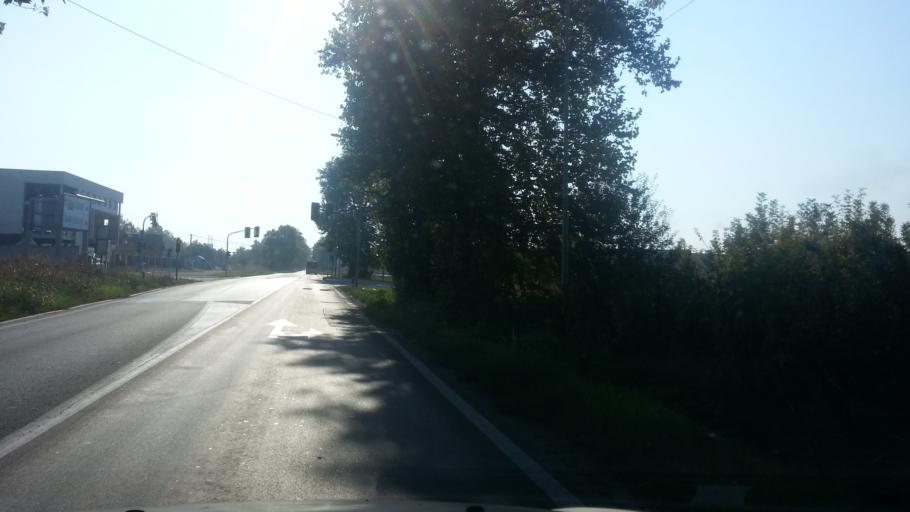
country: RS
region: Central Serbia
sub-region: Belgrade
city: Zemun
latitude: 44.8720
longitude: 20.3481
